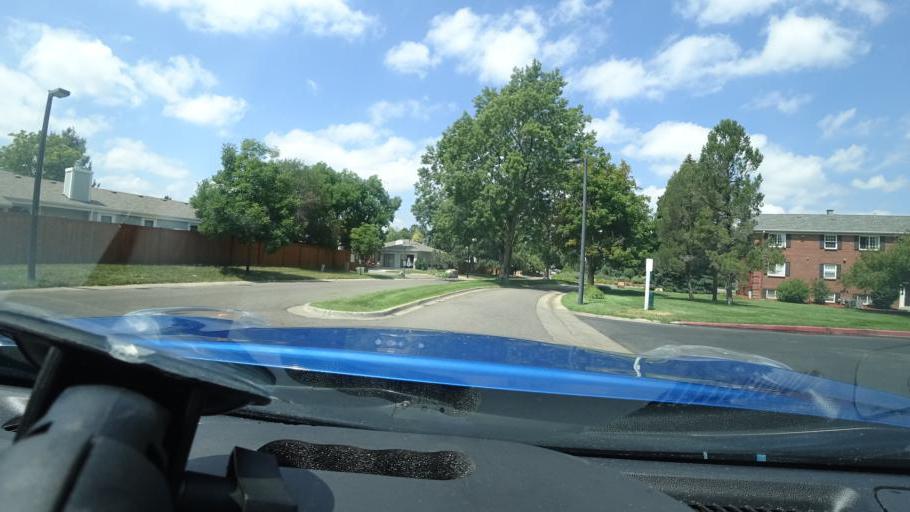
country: US
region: Colorado
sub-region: Adams County
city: Aurora
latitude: 39.7134
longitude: -104.8489
